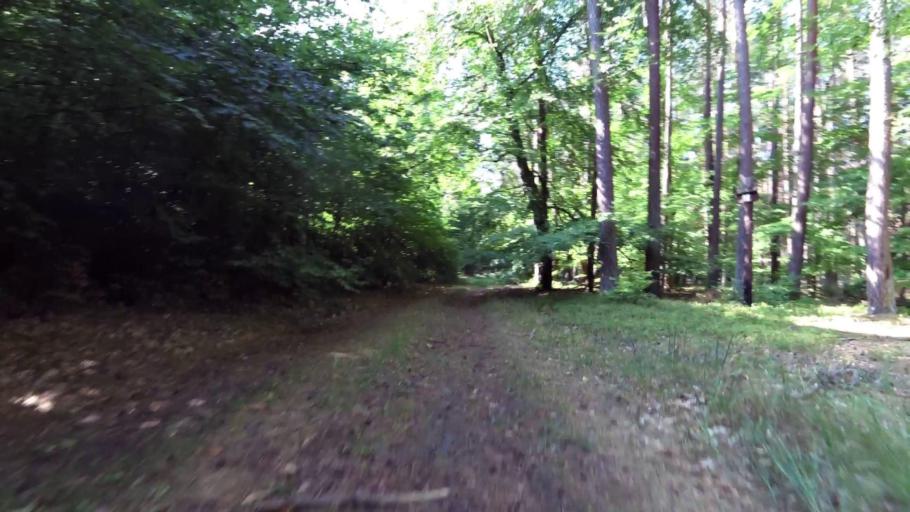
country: PL
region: West Pomeranian Voivodeship
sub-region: Powiat kamienski
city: Miedzyzdroje
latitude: 53.9124
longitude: 14.4843
